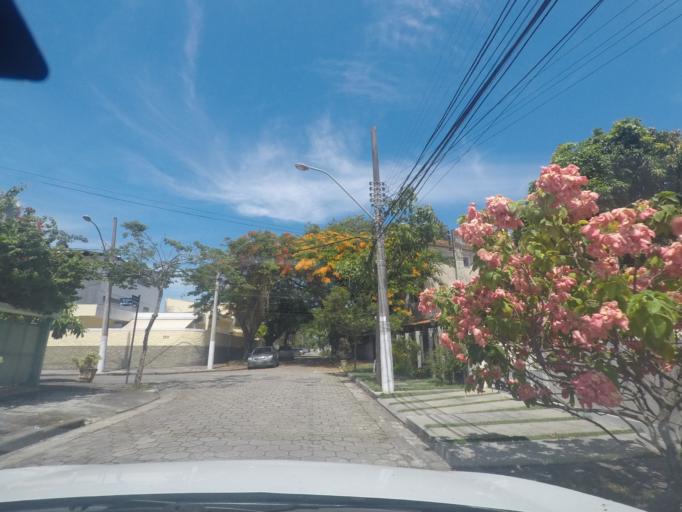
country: BR
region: Rio de Janeiro
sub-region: Niteroi
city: Niteroi
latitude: -22.9160
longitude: -43.0886
